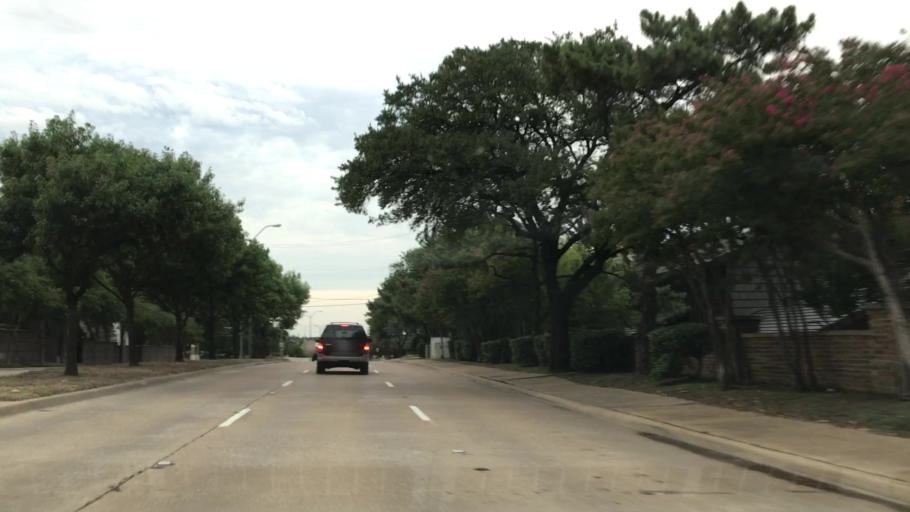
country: US
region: Texas
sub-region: Dallas County
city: Addison
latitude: 32.9201
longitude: -96.7862
